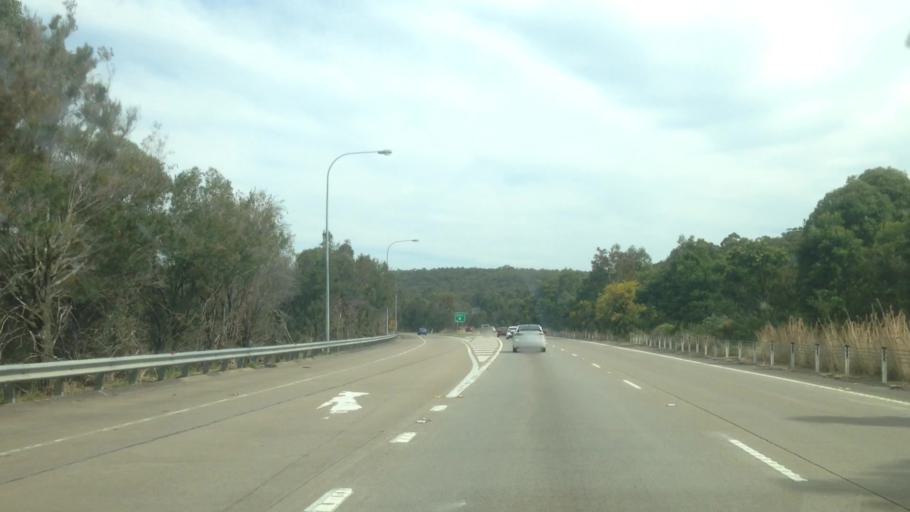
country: AU
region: New South Wales
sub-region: Lake Macquarie Shire
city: Toronto
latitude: -32.9833
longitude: 151.5227
